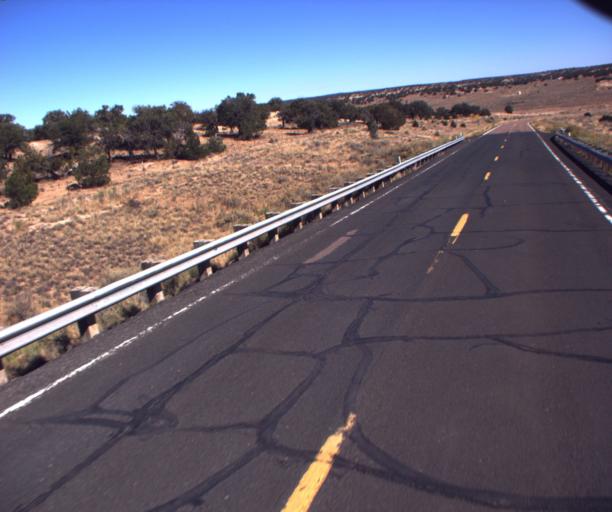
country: US
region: Arizona
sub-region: Navajo County
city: First Mesa
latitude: 35.7660
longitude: -109.9907
